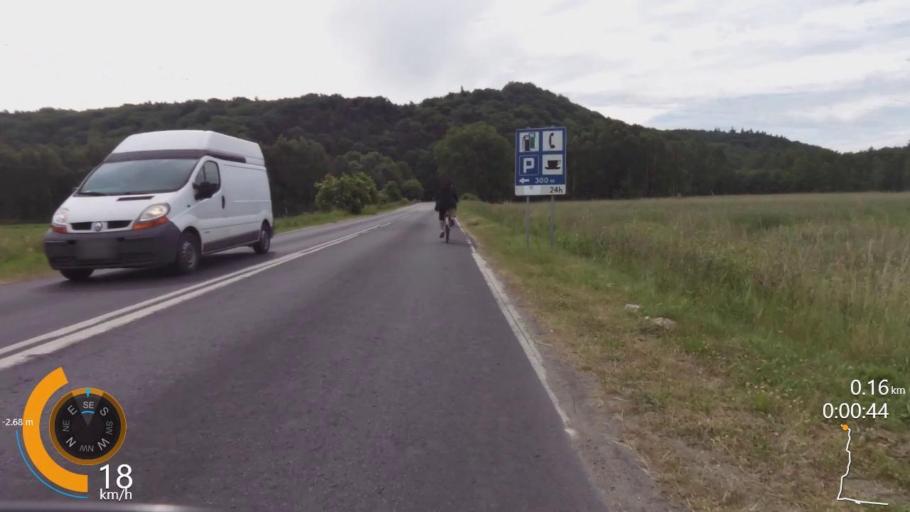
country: PL
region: West Pomeranian Voivodeship
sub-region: Powiat kamienski
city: Miedzyzdroje
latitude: 53.9112
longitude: 14.4353
